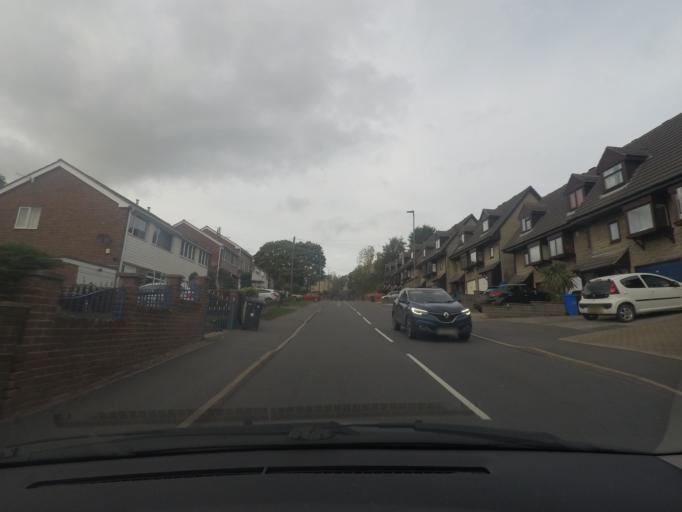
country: GB
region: England
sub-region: Sheffield
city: Oughtibridge
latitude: 53.4218
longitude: -1.4986
